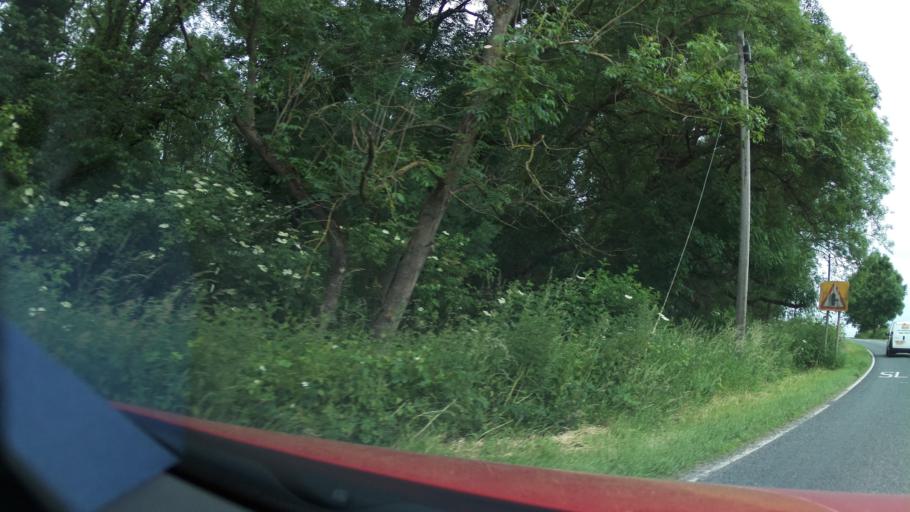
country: GB
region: England
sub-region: Nottinghamshire
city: East Leake
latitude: 52.8181
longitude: -1.2078
